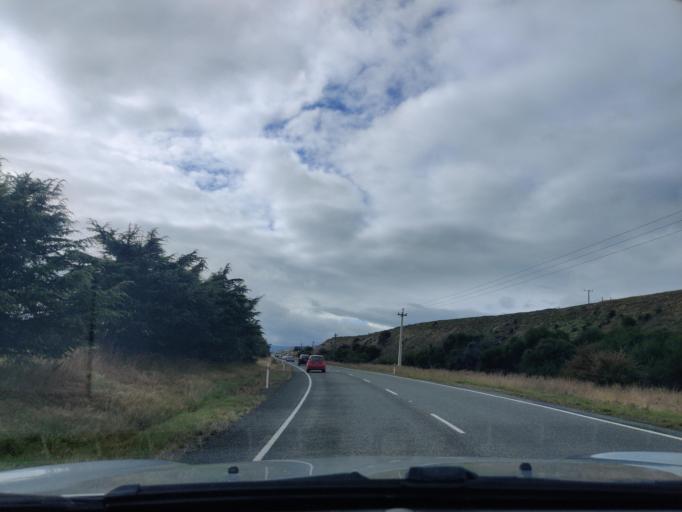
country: NZ
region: Canterbury
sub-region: Hurunui District
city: Amberley
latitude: -42.7000
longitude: 172.8071
